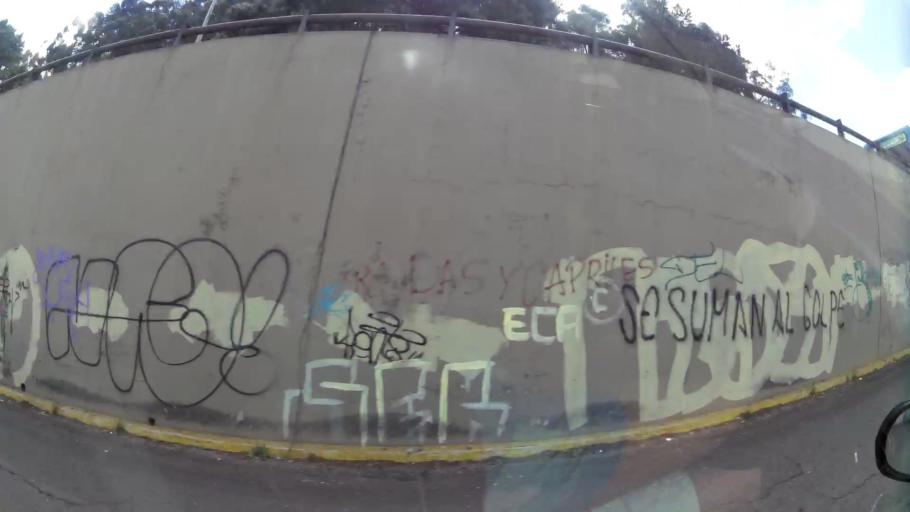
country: EC
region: Pichincha
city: Quito
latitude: -0.2051
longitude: -78.5112
